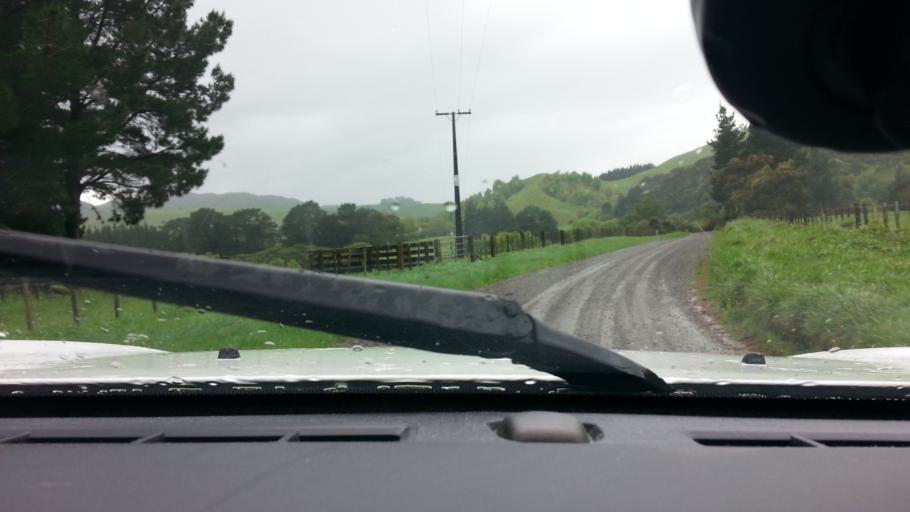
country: NZ
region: Wellington
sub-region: Masterton District
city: Masterton
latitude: -40.9558
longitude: 175.5279
